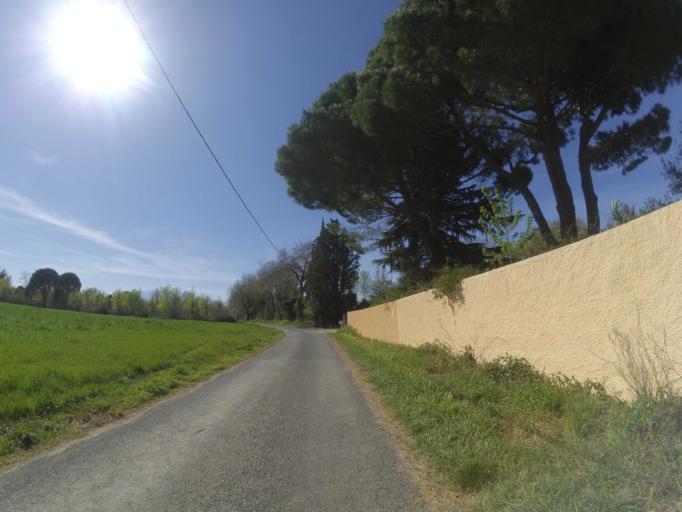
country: FR
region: Languedoc-Roussillon
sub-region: Departement des Pyrenees-Orientales
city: Le Soler
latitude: 42.6745
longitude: 2.8026
